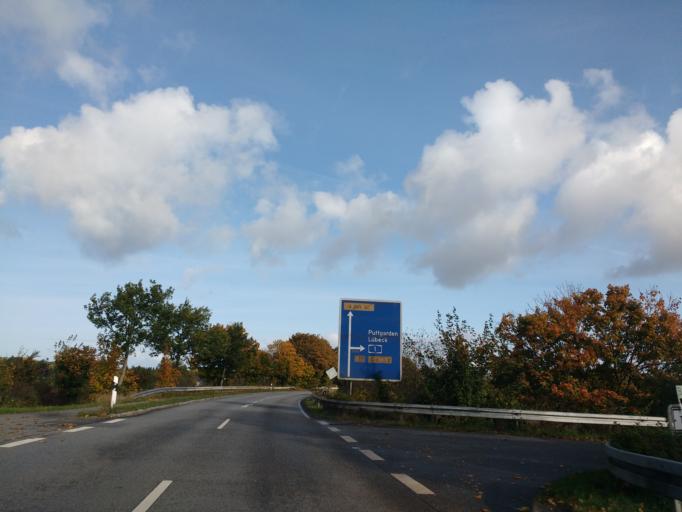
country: DE
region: Schleswig-Holstein
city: Altenkrempe
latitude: 54.1277
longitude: 10.8213
